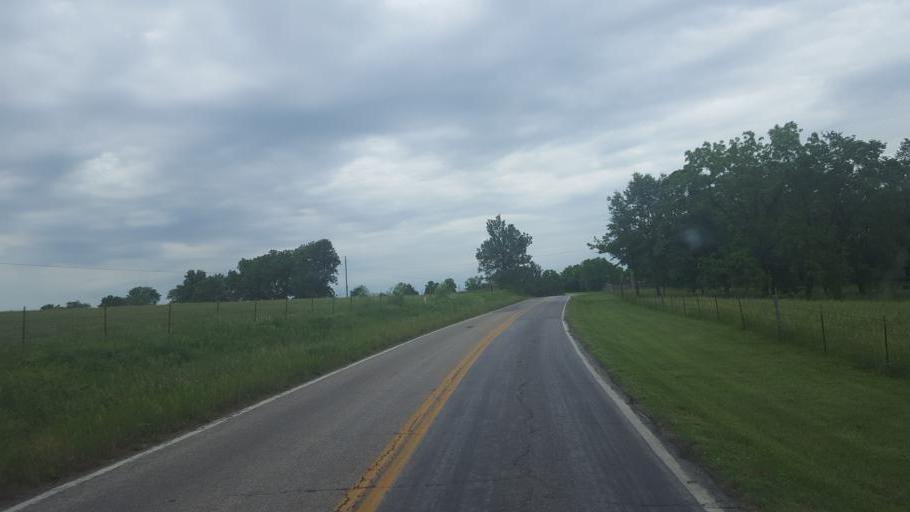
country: US
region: Missouri
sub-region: Moniteau County
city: California
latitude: 38.6637
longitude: -92.5821
